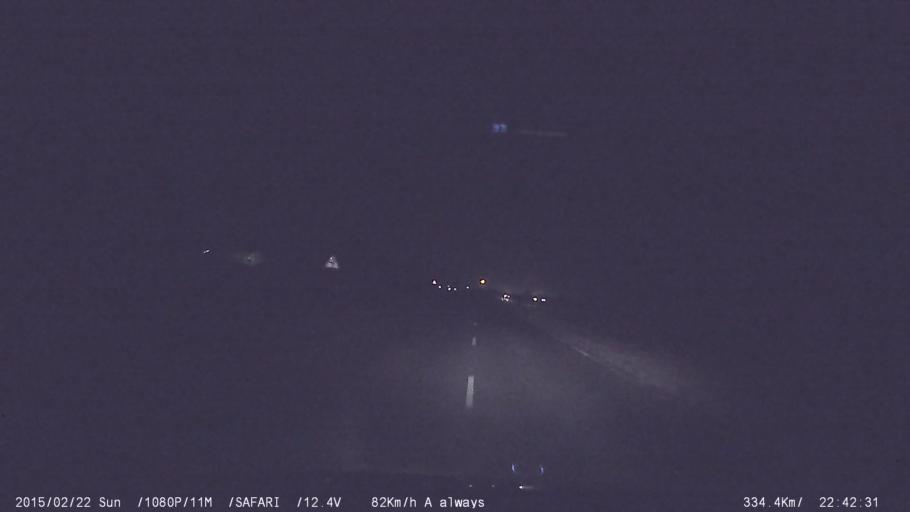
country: IN
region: Tamil Nadu
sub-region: Namakkal
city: Namakkal
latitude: 11.1886
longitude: 78.0830
